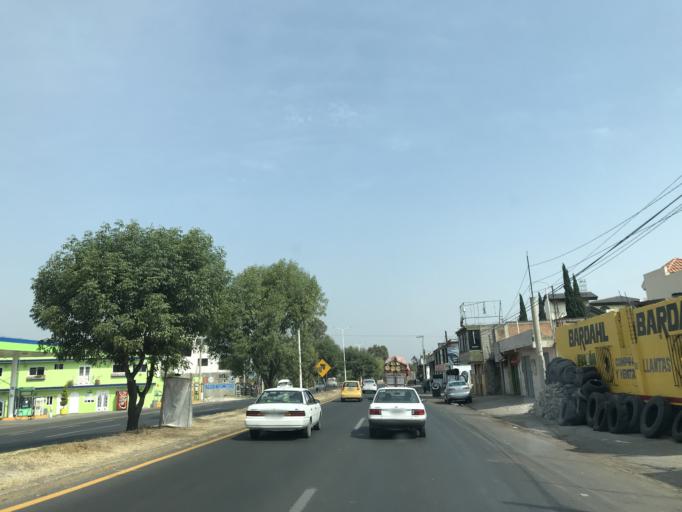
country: MX
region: Tlaxcala
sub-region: Teolocholco
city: Teolocholco
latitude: 19.2537
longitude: -98.1983
